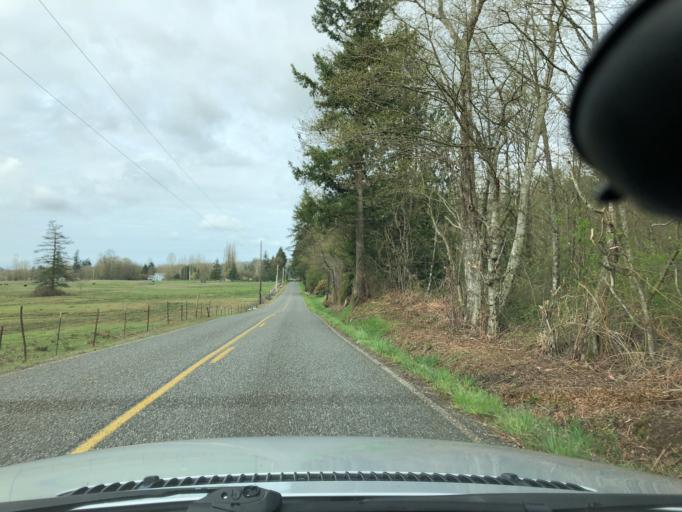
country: CA
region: British Columbia
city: Langley
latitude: 48.9792
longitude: -122.5884
